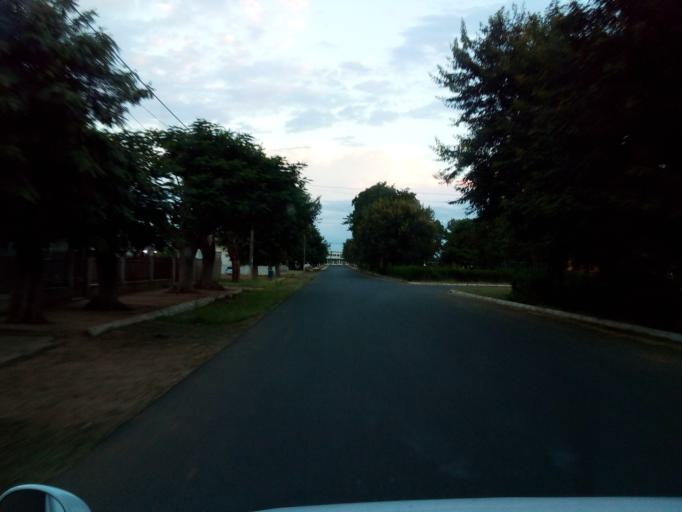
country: MZ
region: Maputo City
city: Maputo
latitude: -26.3438
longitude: 32.6758
